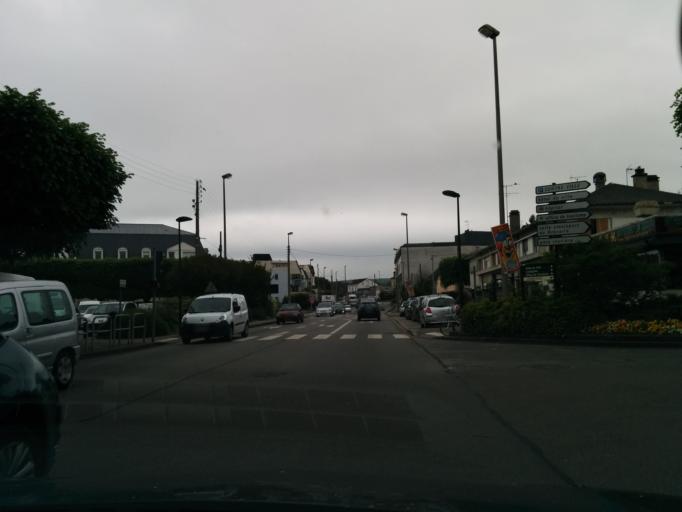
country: FR
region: Haute-Normandie
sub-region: Departement de l'Eure
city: Vernon
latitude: 49.0925
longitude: 1.4885
